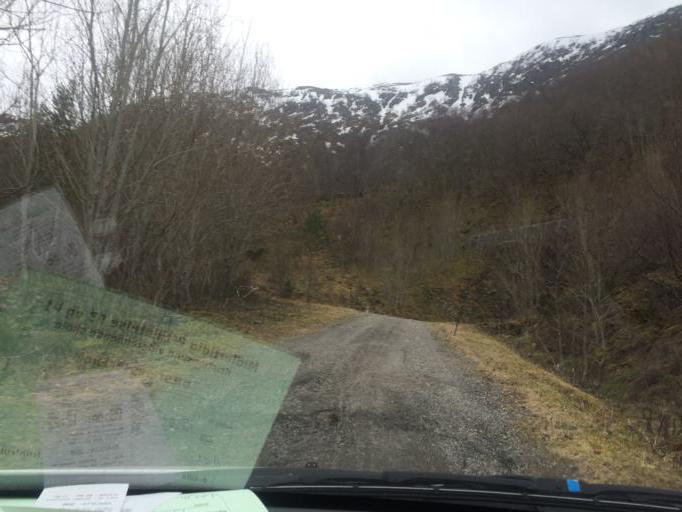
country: NO
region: More og Romsdal
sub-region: Gjemnes
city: Batnfjordsora
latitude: 62.9651
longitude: 7.7326
